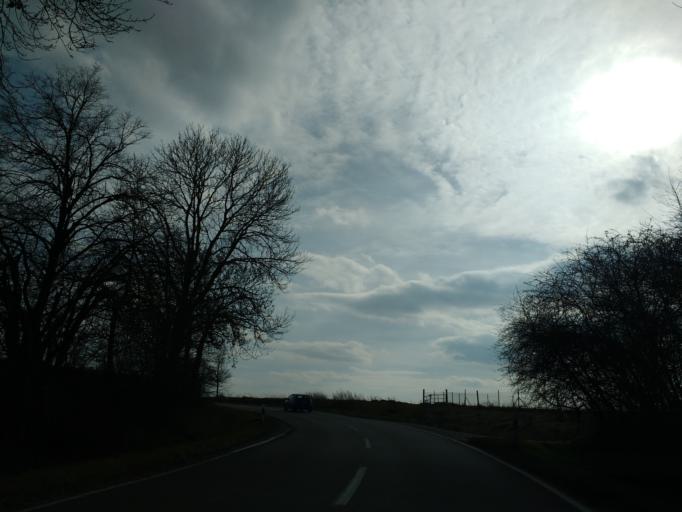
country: DE
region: Saxony-Anhalt
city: Schraplau
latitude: 51.4297
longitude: 11.6494
